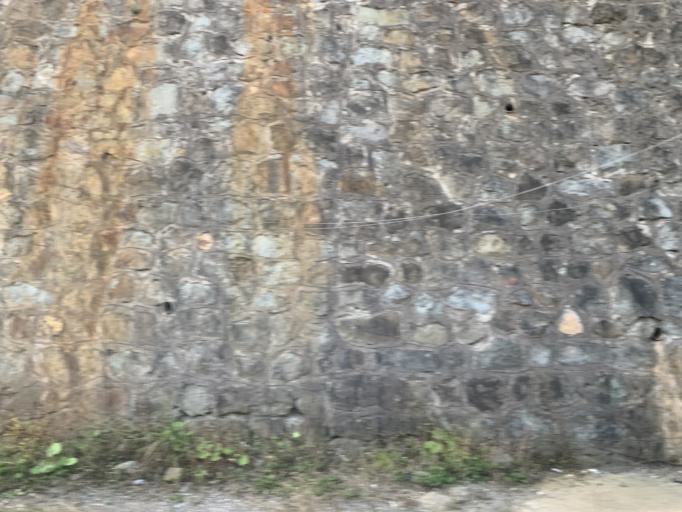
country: TR
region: Trabzon
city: Dernekpazari
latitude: 40.8332
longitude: 40.2701
